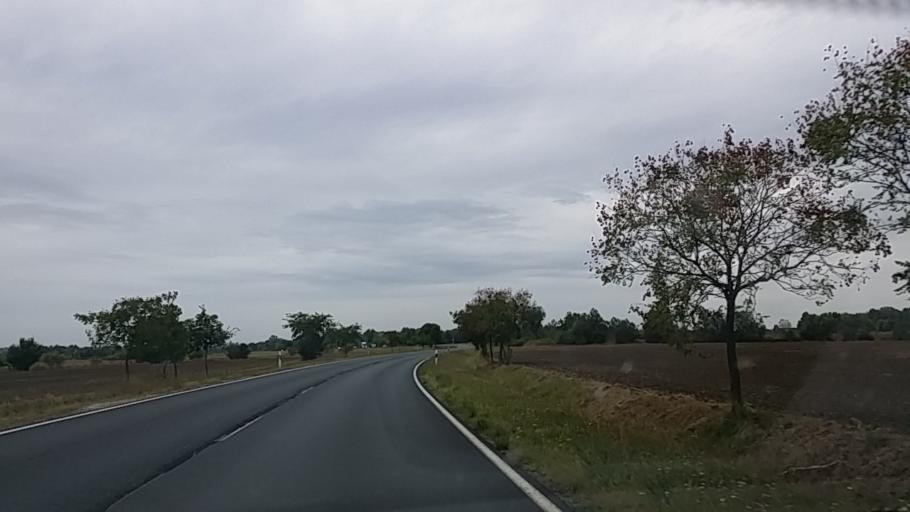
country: HU
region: Gyor-Moson-Sopron
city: Fertoszentmiklos
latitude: 47.5902
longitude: 16.8525
